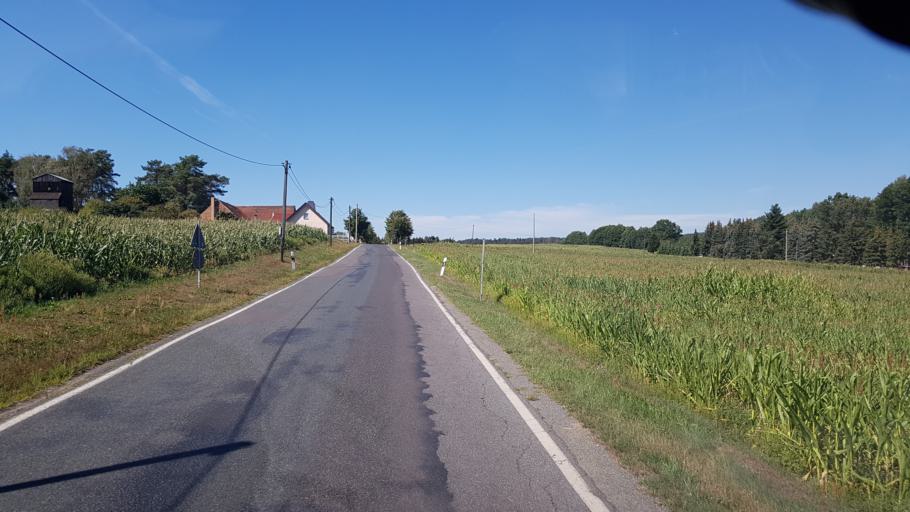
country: DE
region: Brandenburg
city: Bronkow
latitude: 51.6870
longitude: 13.9592
